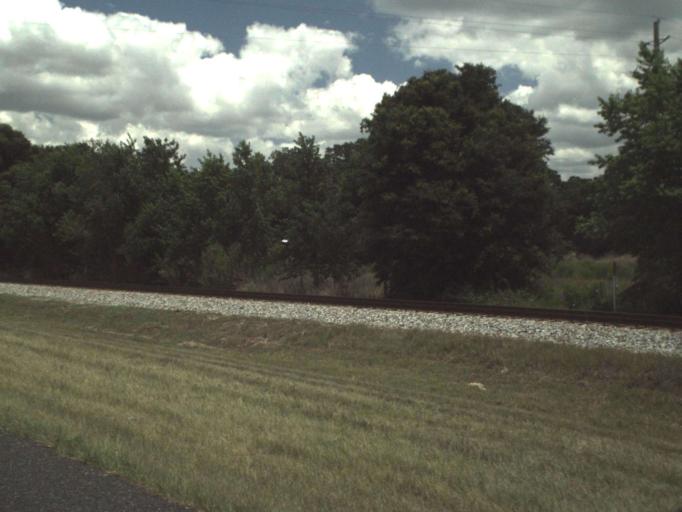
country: US
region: Florida
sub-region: Sumter County
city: The Villages
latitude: 28.9528
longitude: -82.0392
